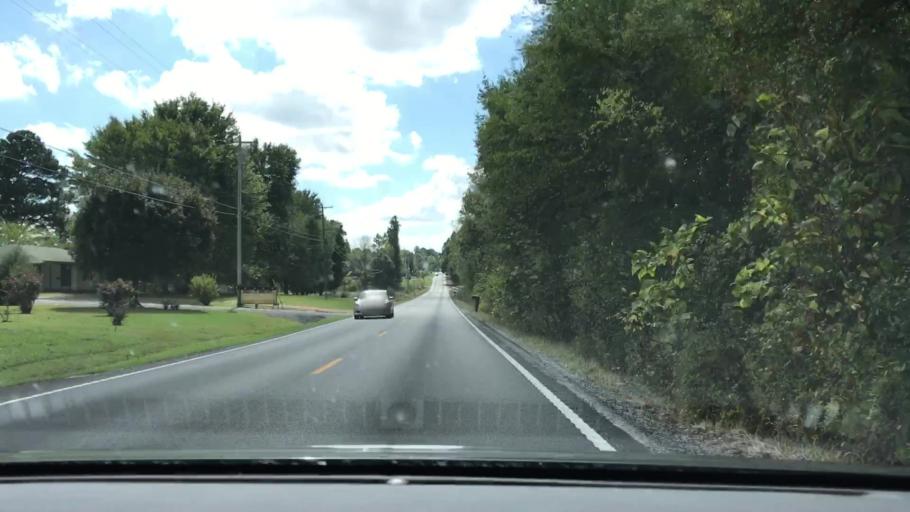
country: US
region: Kentucky
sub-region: Graves County
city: Mayfield
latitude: 36.7875
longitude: -88.5957
